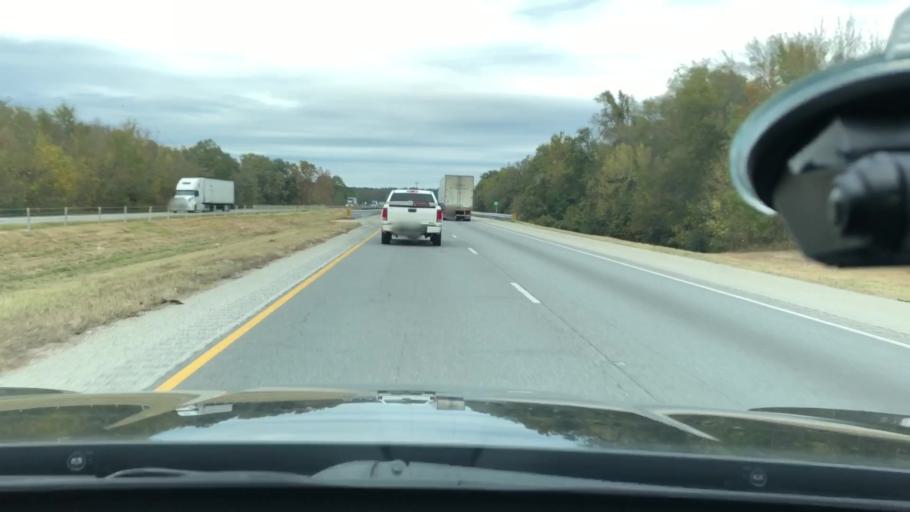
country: US
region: Arkansas
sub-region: Clark County
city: Arkadelphia
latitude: 34.1731
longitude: -93.0746
